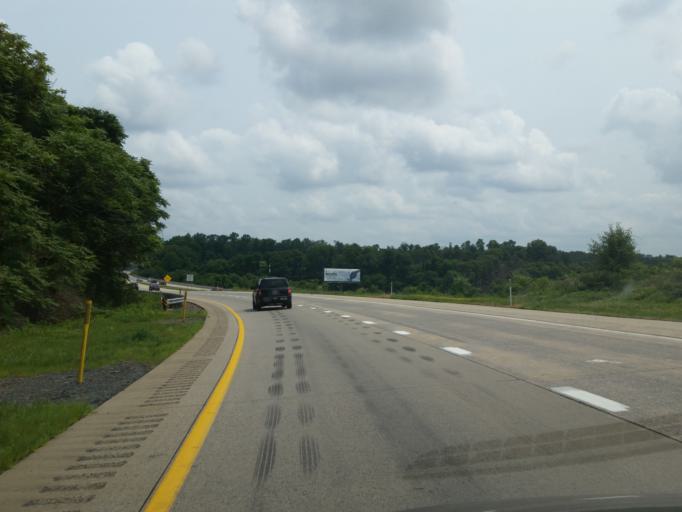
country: US
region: Pennsylvania
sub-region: Dauphin County
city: Progress
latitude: 40.3073
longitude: -76.8338
